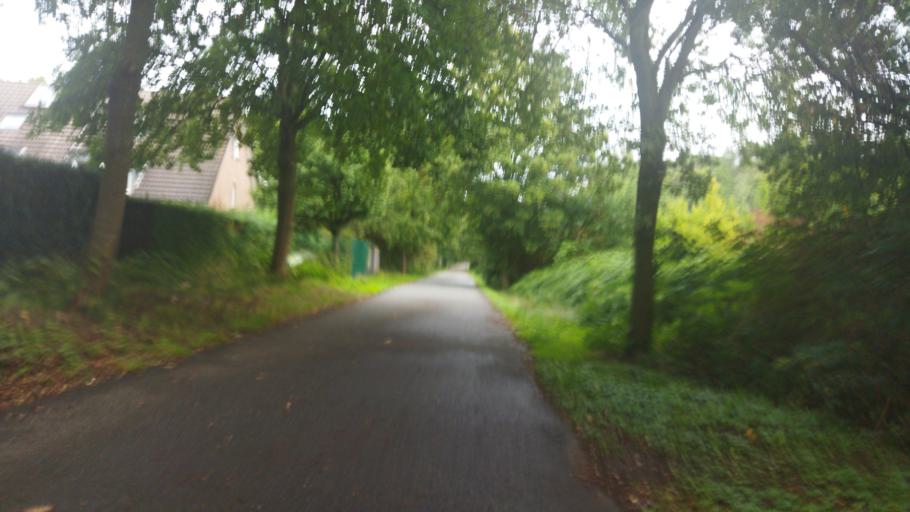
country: DE
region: North Rhine-Westphalia
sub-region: Regierungsbezirk Munster
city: Gelsenkirchen
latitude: 51.4862
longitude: 7.1071
